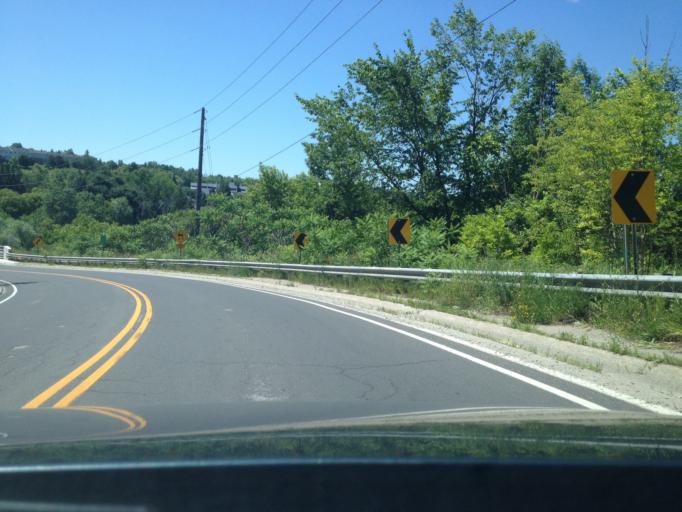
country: CA
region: Ontario
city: Brampton
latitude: 43.6633
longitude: -79.9085
